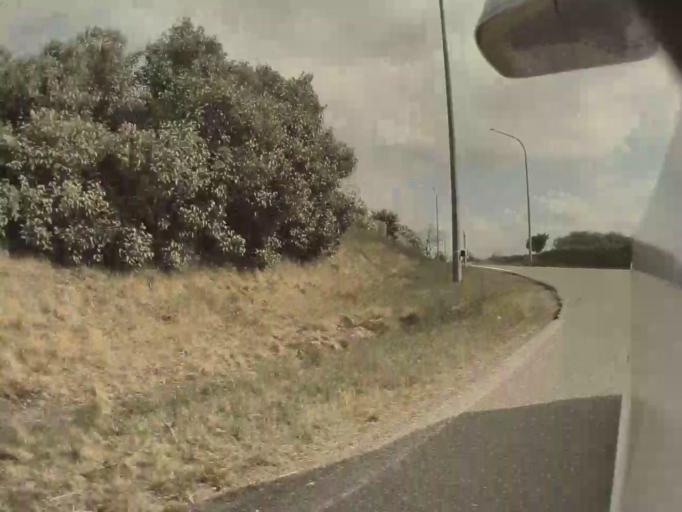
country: BE
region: Wallonia
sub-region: Province de Namur
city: Somme-Leuze
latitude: 50.3163
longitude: 5.3410
